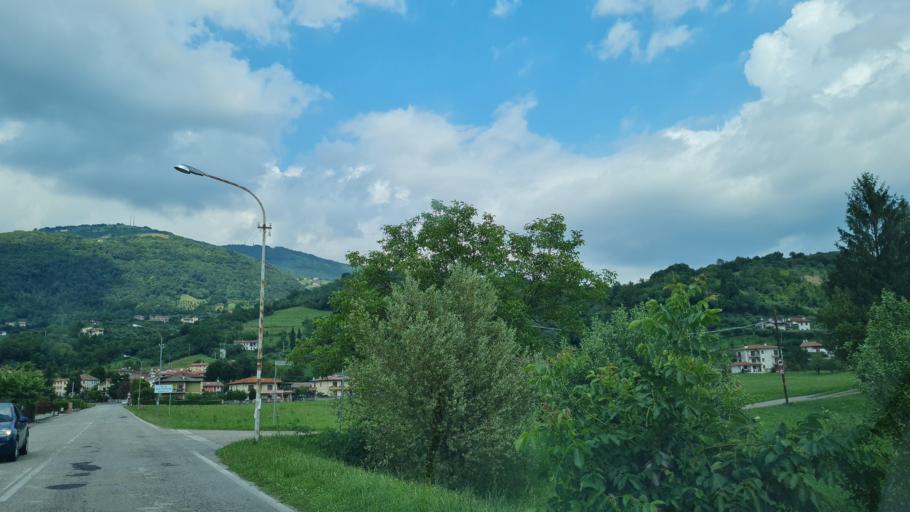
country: IT
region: Veneto
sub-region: Provincia di Vicenza
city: Marostica
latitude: 45.7652
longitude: 11.6606
